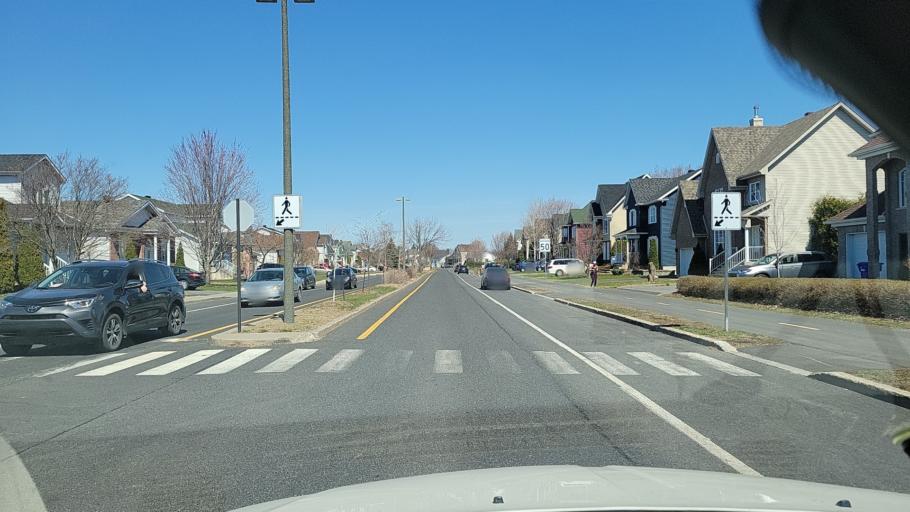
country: CA
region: Quebec
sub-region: Monteregie
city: Sainte-Julie
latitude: 45.5842
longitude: -73.3444
